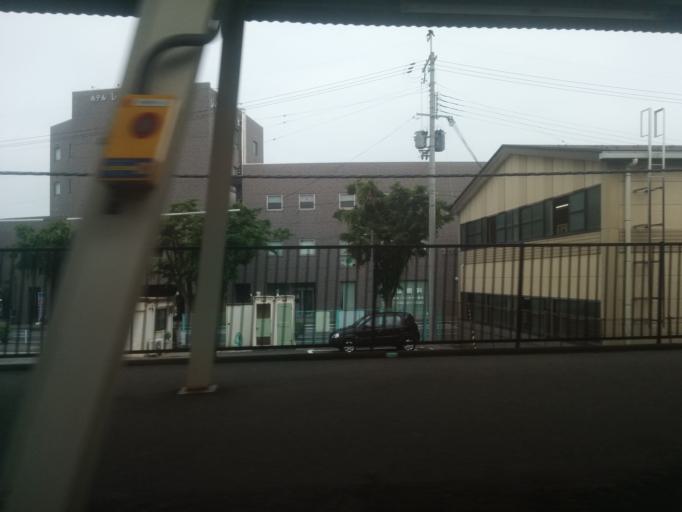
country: JP
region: Shiga Prefecture
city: Hikone
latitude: 35.2458
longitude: 136.2477
